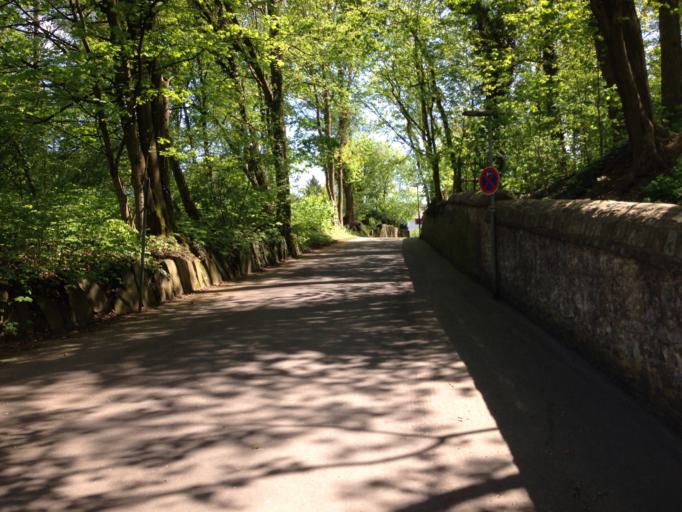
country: DE
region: Hesse
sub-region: Regierungsbezirk Giessen
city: Laubach
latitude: 50.5441
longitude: 8.9939
